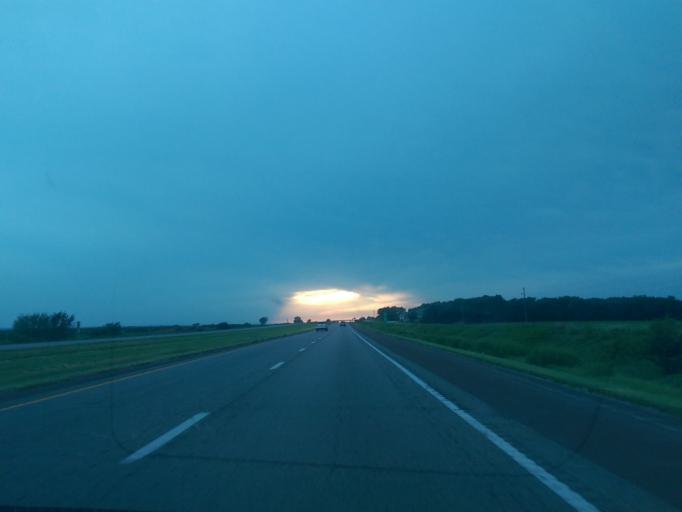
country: US
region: Missouri
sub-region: Holt County
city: Mound City
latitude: 40.1541
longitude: -95.2588
